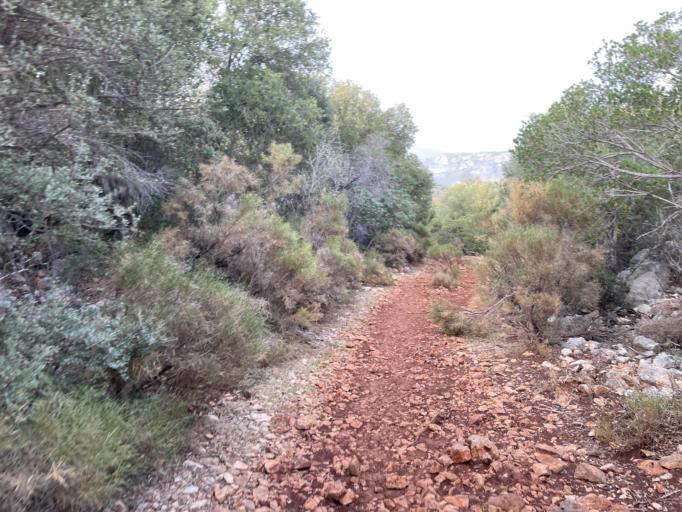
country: TR
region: Antalya
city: Kas
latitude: 36.1639
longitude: 29.6541
